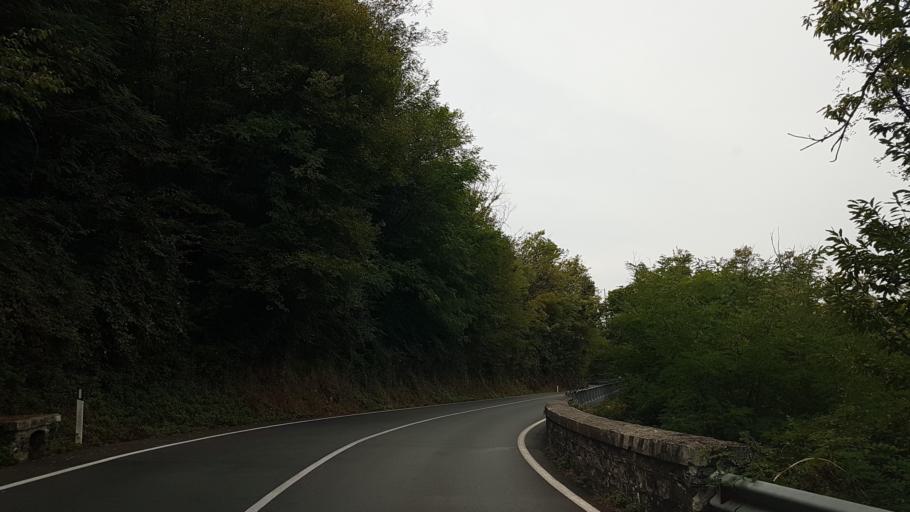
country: IT
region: Liguria
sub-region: Provincia di Genova
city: Casarza Ligure
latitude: 44.2614
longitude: 9.4504
